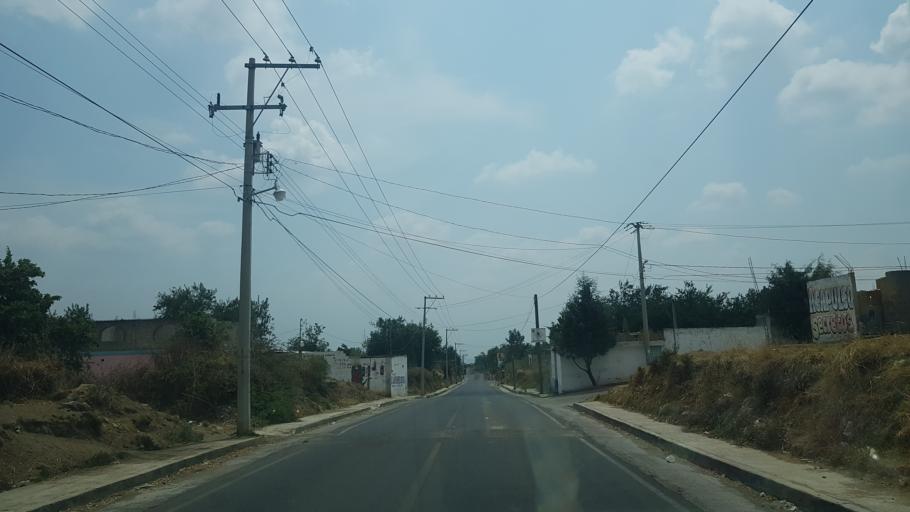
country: MX
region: Puebla
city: Domingo Arenas
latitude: 19.1409
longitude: -98.4658
